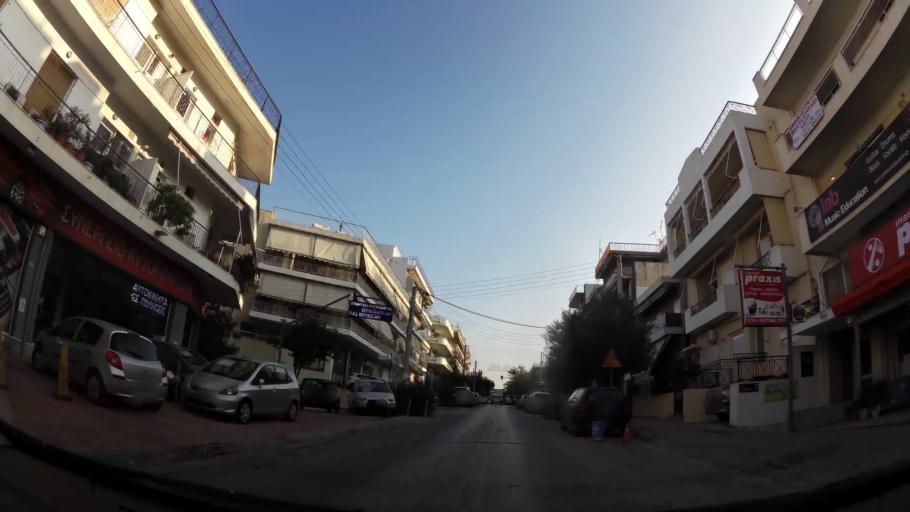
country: GR
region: Attica
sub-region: Nomarchia Athinas
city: Agios Dimitrios
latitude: 37.9388
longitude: 23.7429
